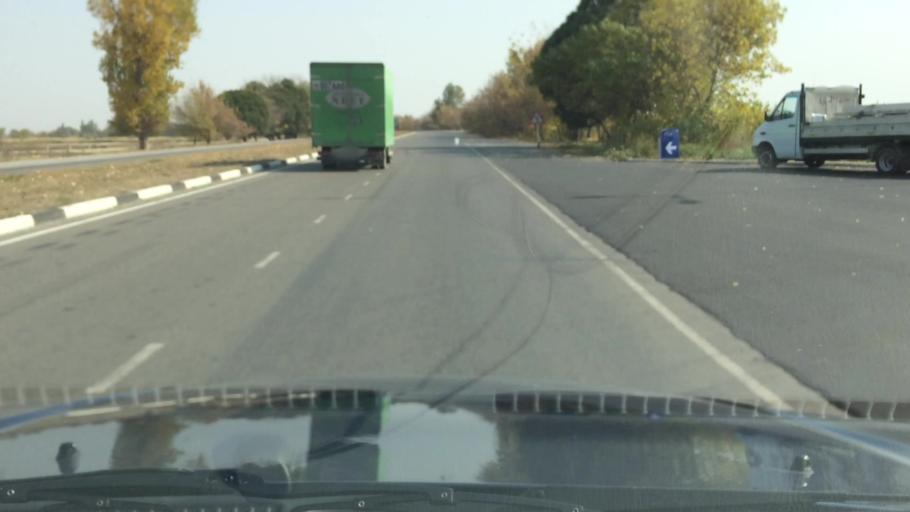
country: KG
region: Chuy
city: Lebedinovka
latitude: 42.9228
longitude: 74.7549
